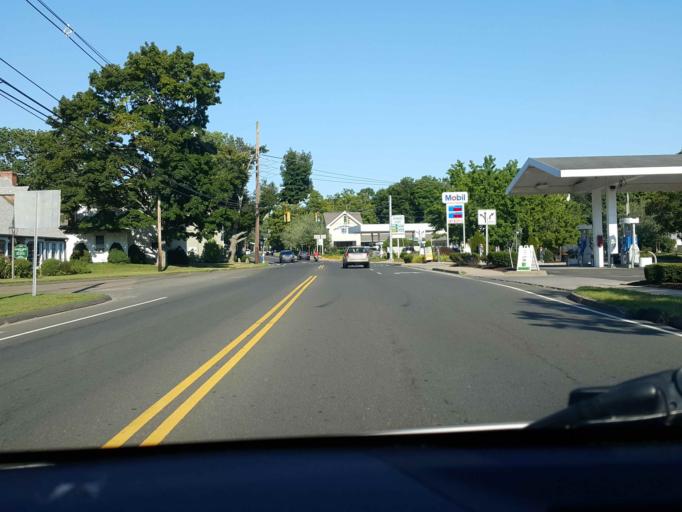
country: US
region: Connecticut
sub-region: New Haven County
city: Guilford
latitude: 41.2876
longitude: -72.6894
